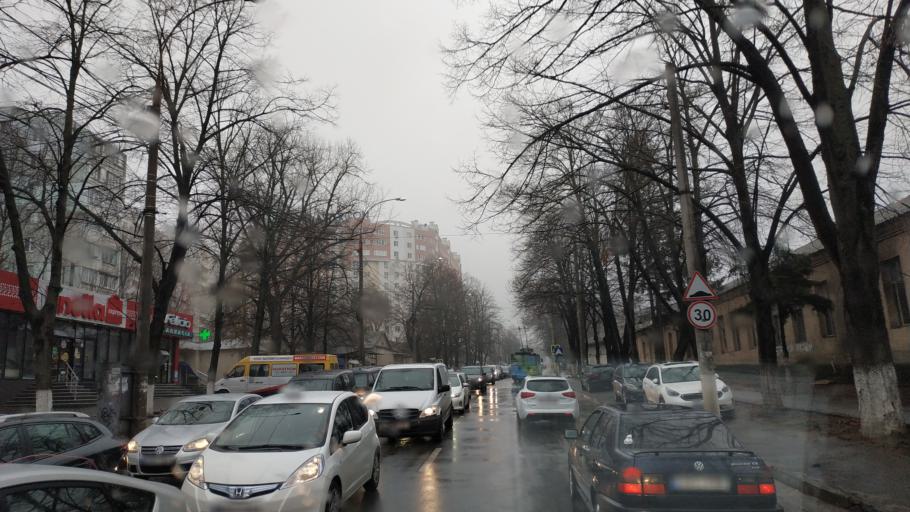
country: MD
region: Chisinau
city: Chisinau
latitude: 47.0219
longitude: 28.8014
